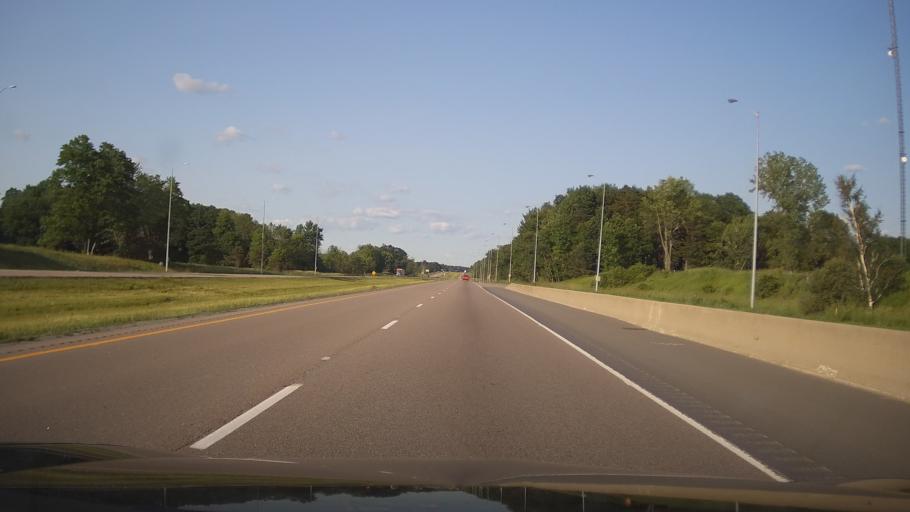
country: CA
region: Ontario
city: Gananoque
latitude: 44.3615
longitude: -76.0788
